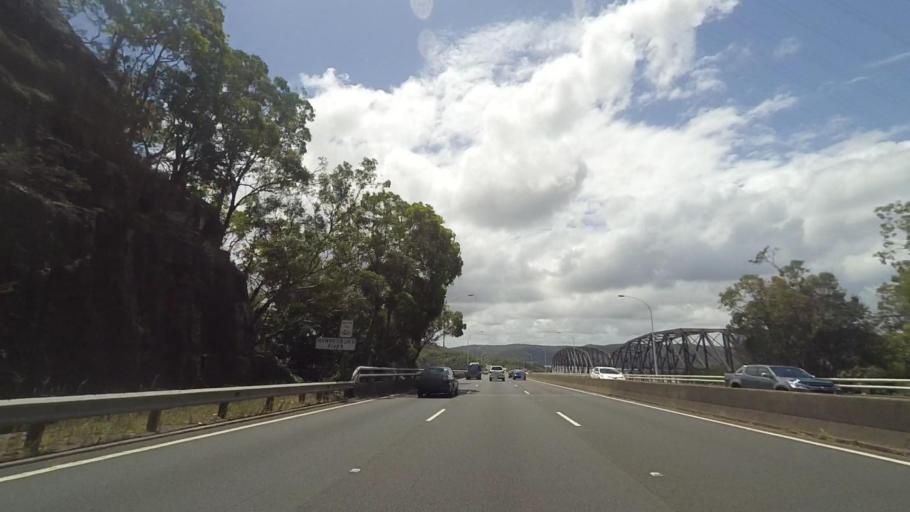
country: AU
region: New South Wales
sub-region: Hornsby Shire
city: Berowra
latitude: -33.5416
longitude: 151.1980
